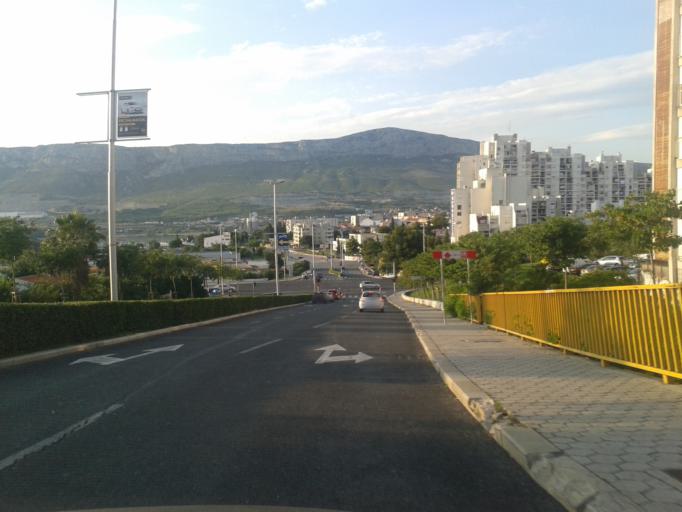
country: HR
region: Splitsko-Dalmatinska
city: Vranjic
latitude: 43.5187
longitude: 16.4620
